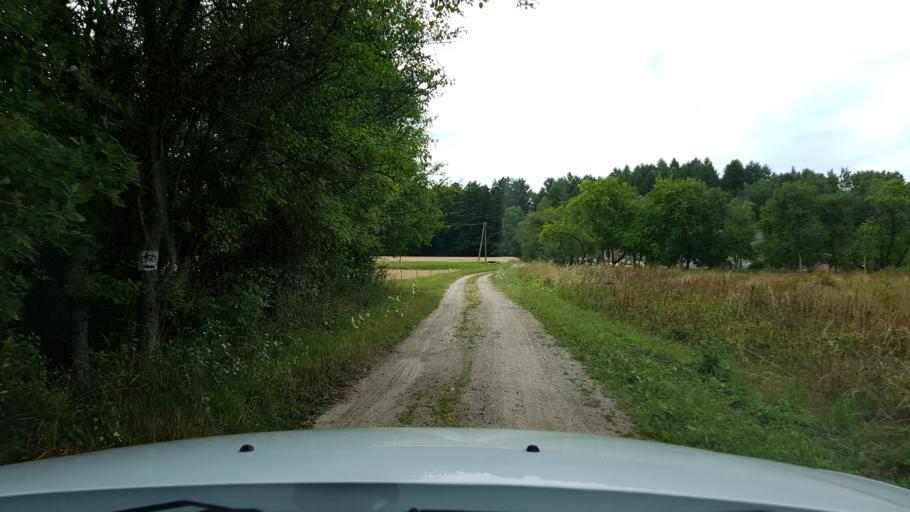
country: PL
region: West Pomeranian Voivodeship
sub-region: Powiat drawski
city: Wierzchowo
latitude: 53.4767
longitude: 16.1254
